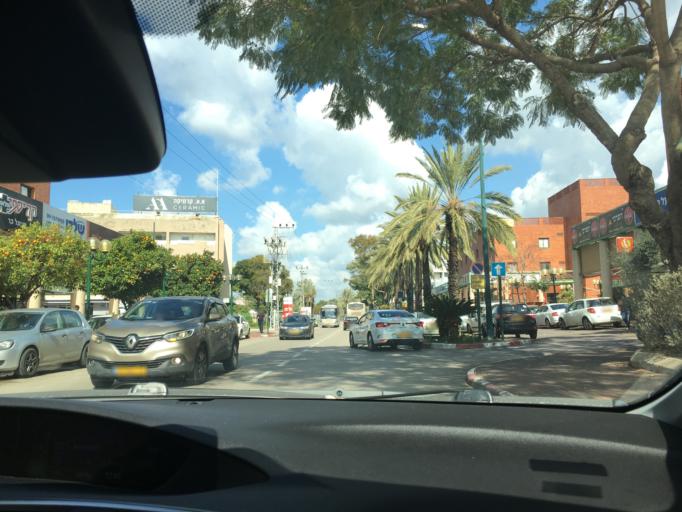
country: IL
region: Central District
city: Kfar Saba
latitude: 32.1770
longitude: 34.9274
